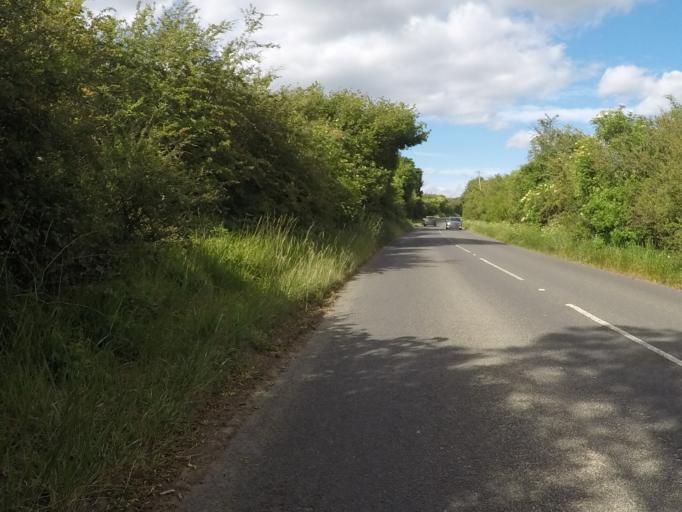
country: GB
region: England
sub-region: Oxfordshire
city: Charlbury
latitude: 51.8331
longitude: -1.5016
